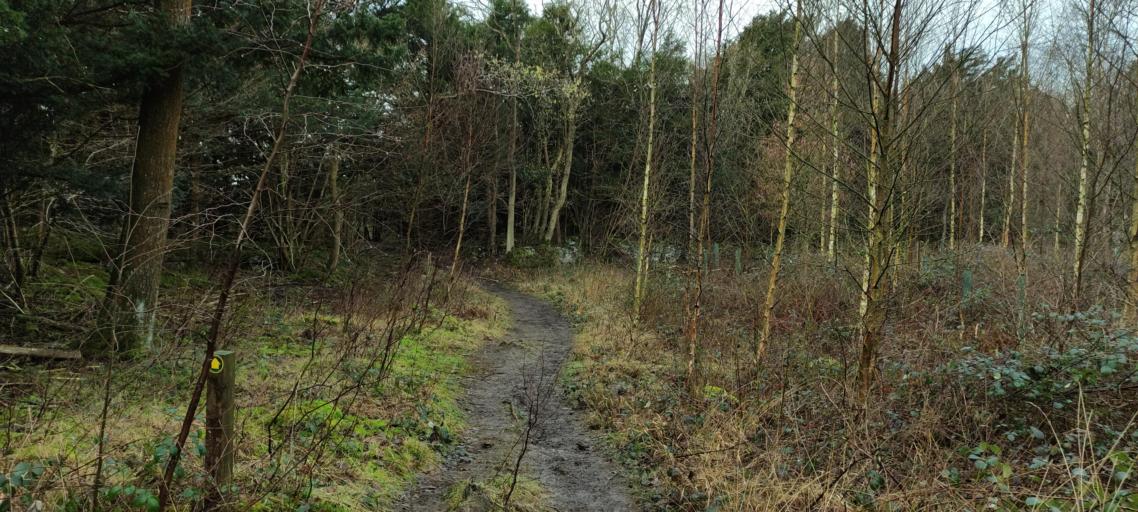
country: GB
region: England
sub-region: Cumbria
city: Milnthorpe
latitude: 54.2007
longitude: -2.7713
